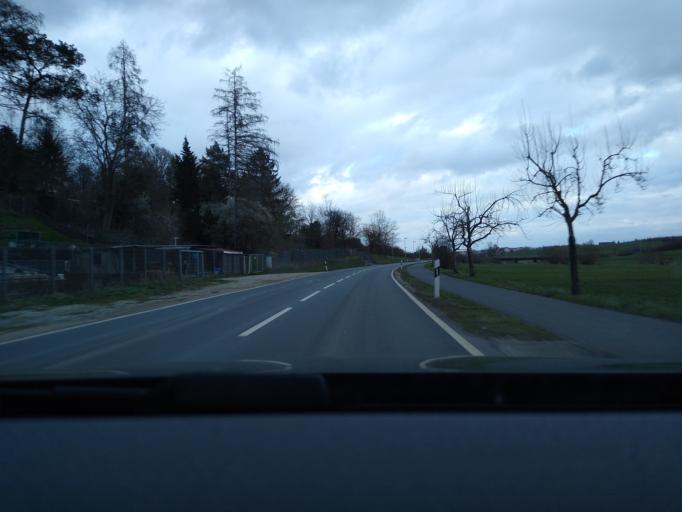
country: DE
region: Bavaria
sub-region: Regierungsbezirk Mittelfranken
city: Zirndorf
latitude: 49.4474
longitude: 10.9302
